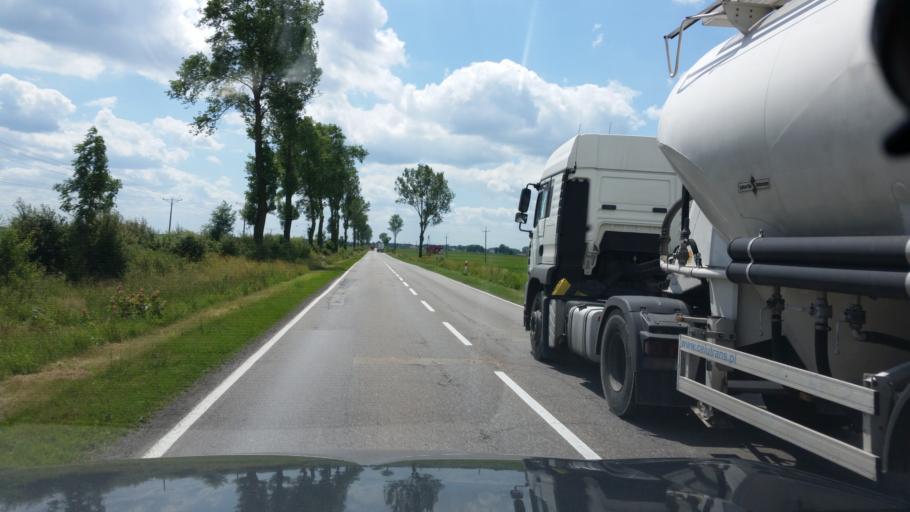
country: PL
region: Podlasie
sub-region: Powiat lomzynski
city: Sniadowo
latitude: 53.0872
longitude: 22.0208
